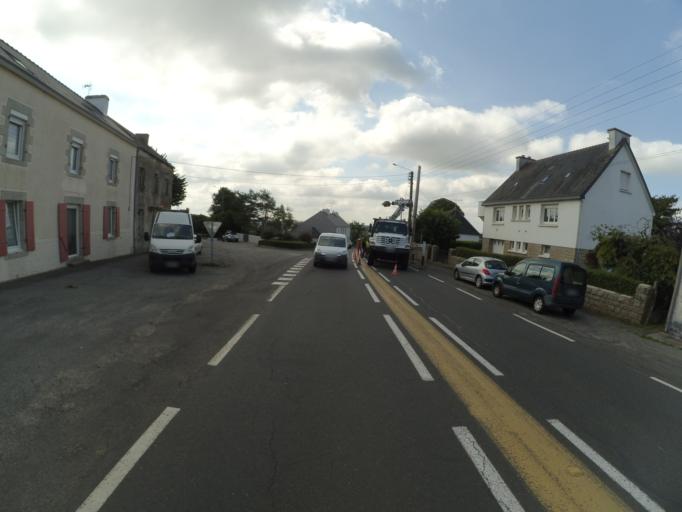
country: FR
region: Brittany
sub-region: Departement du Finistere
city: Quimperle
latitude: 47.8869
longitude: -3.5602
